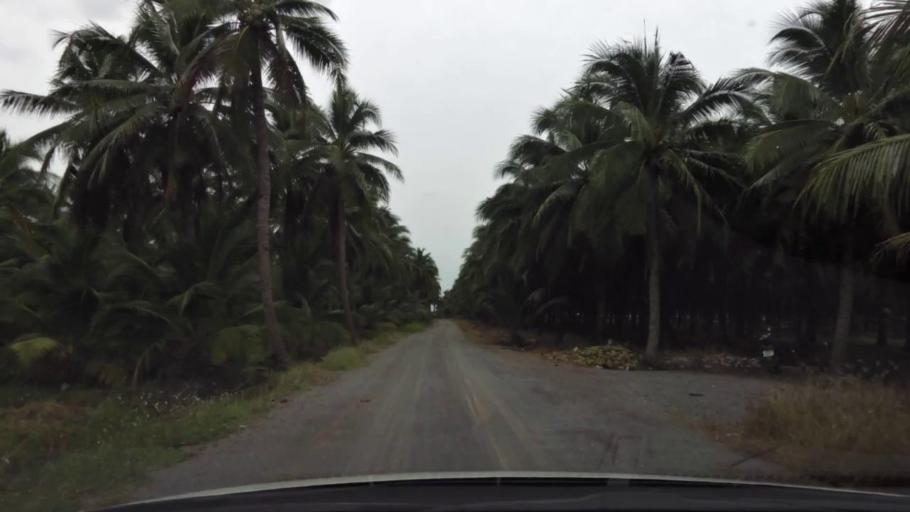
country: TH
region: Samut Sakhon
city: Ban Phaeo
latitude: 13.6139
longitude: 100.0273
